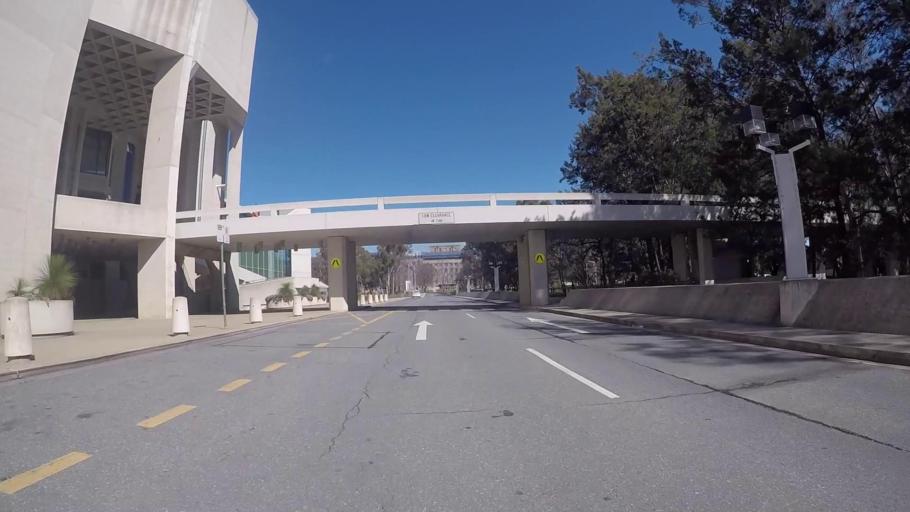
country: AU
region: Australian Capital Territory
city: Forrest
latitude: -35.3000
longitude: 149.1363
